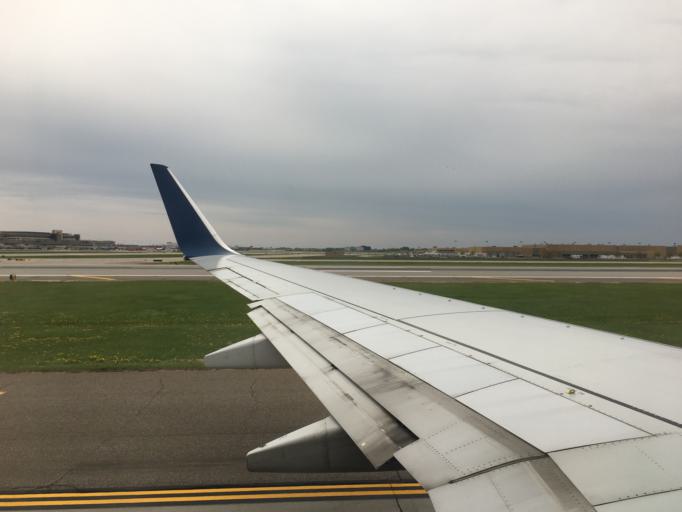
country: US
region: Minnesota
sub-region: Hennepin County
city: Richfield
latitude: 44.8850
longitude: -93.2245
